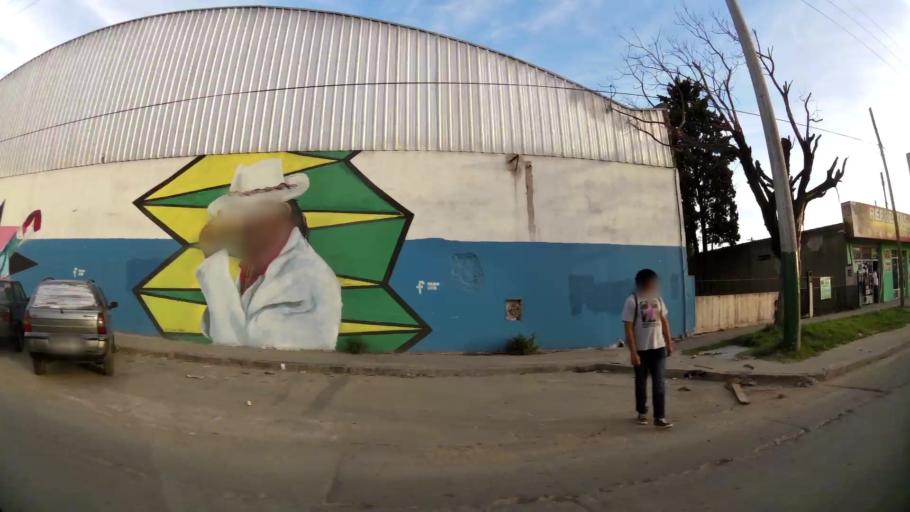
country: AR
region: Buenos Aires
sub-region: Partido de Almirante Brown
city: Adrogue
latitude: -34.7775
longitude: -58.3315
